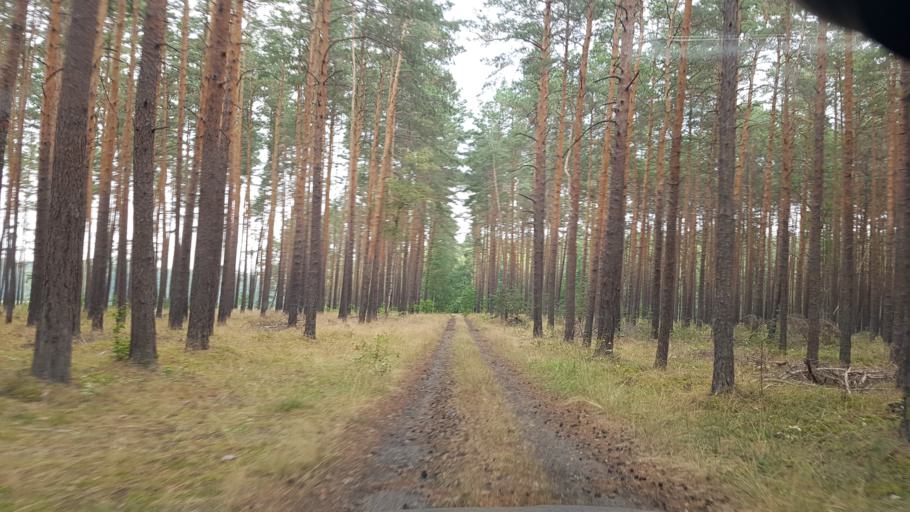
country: DE
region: Saxony
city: Bernsdorf
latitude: 51.3695
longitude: 14.0925
